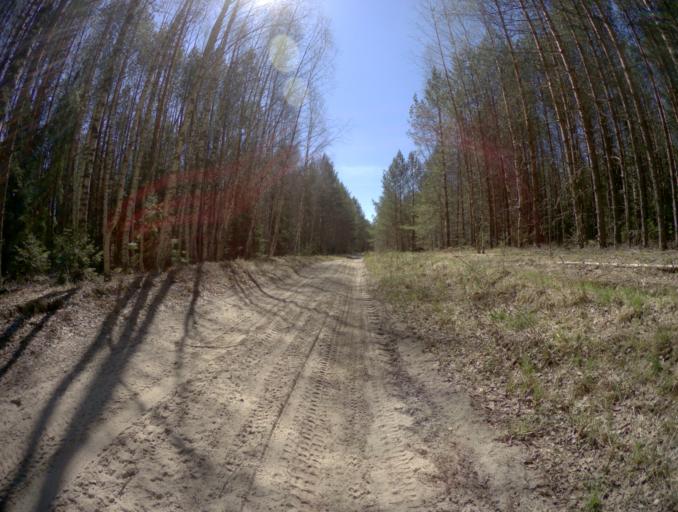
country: RU
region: Vladimir
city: Golovino
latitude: 55.8883
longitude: 40.4082
